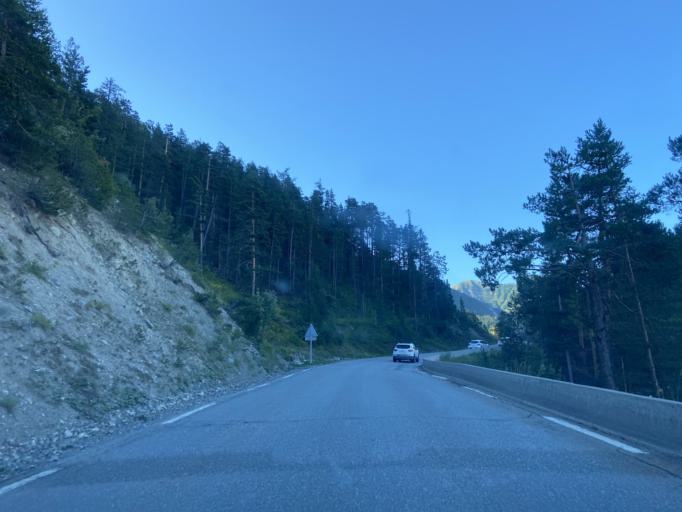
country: IT
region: Piedmont
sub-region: Provincia di Torino
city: Claviere
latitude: 44.9291
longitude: 6.6948
